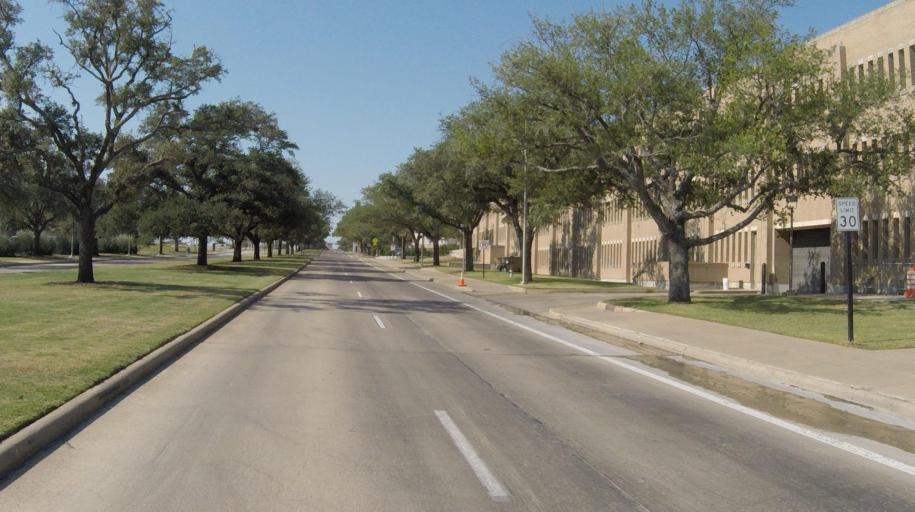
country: US
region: Texas
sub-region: Brazos County
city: College Station
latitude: 30.6134
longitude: -96.3324
